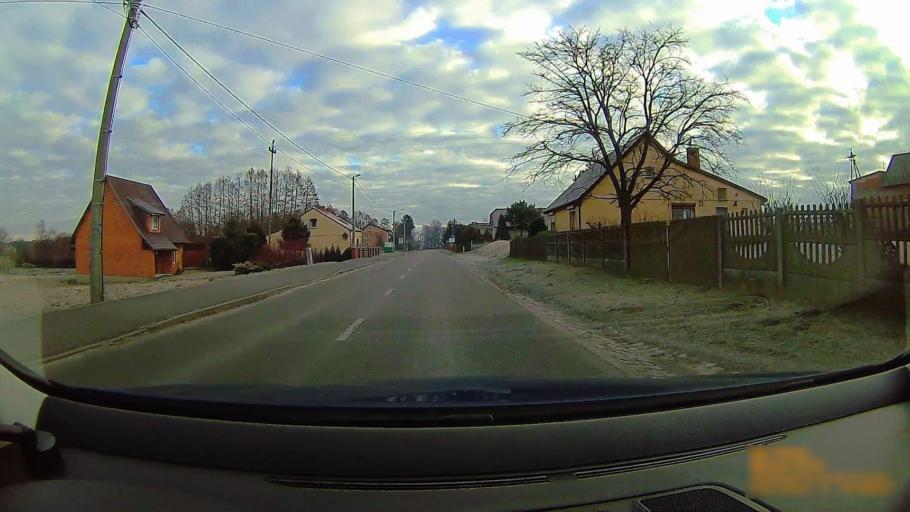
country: PL
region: Greater Poland Voivodeship
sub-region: Powiat koninski
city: Rzgow Pierwszy
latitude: 52.1767
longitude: 18.0959
